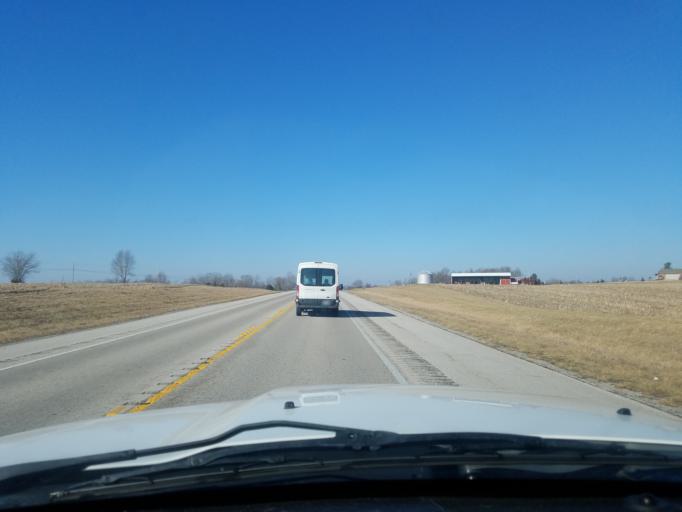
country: US
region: Kentucky
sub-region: Green County
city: Greensburg
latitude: 37.4147
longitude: -85.4979
